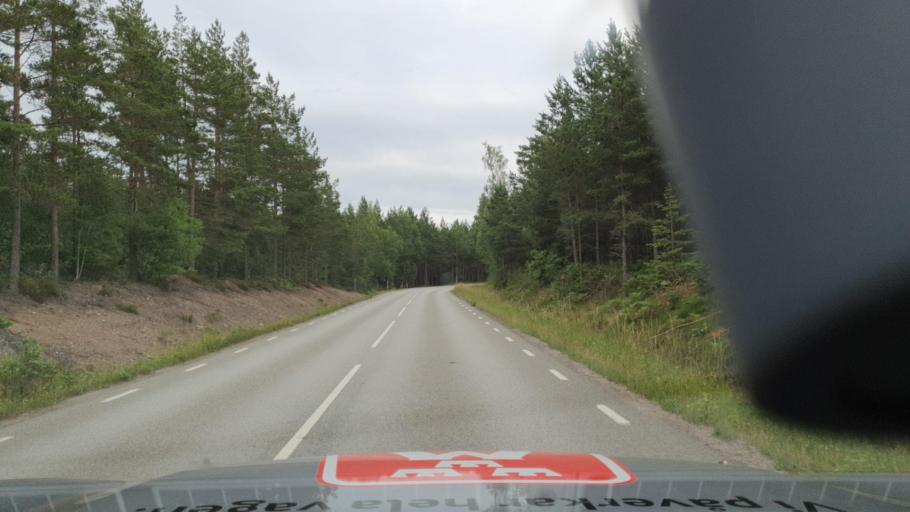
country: SE
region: Kalmar
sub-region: Nybro Kommun
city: Nybro
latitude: 56.6703
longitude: 15.9923
